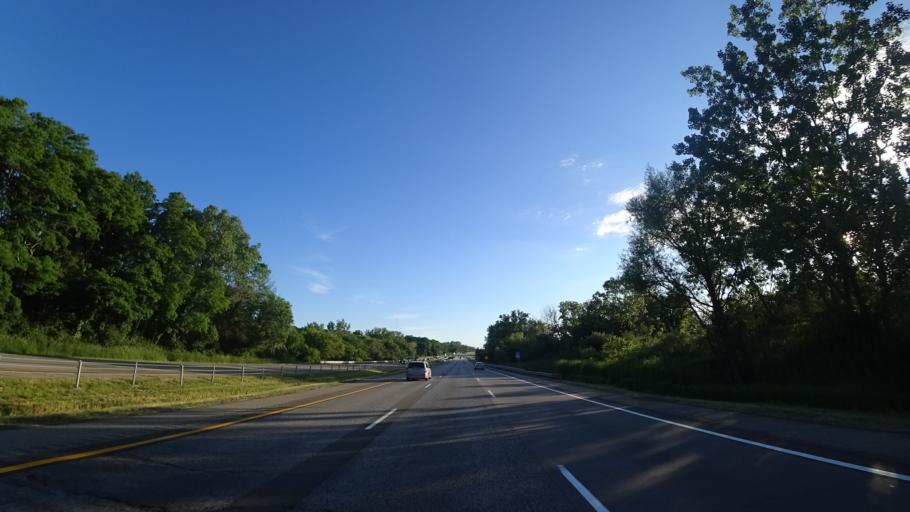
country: US
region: Michigan
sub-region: Berrien County
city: Fair Plain
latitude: 42.0643
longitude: -86.4449
